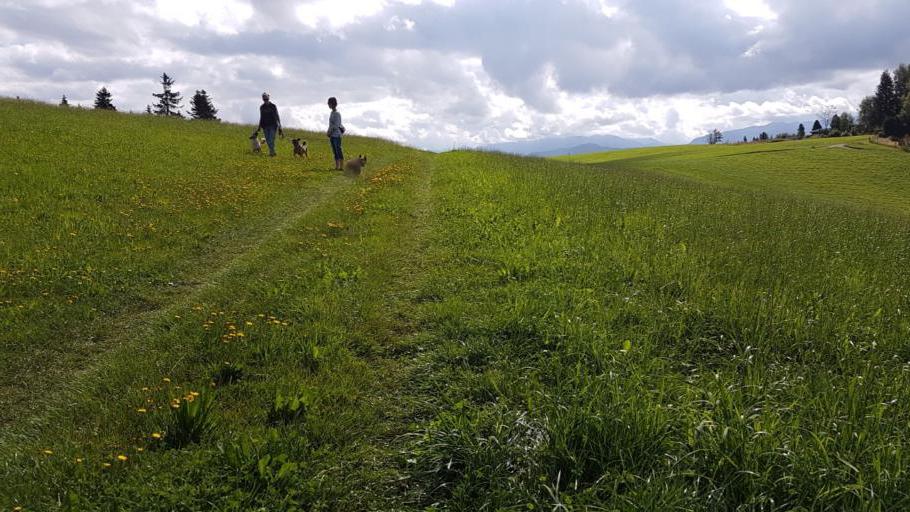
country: CH
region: Bern
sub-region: Bern-Mittelland District
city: Linden
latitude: 46.8590
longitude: 7.6701
